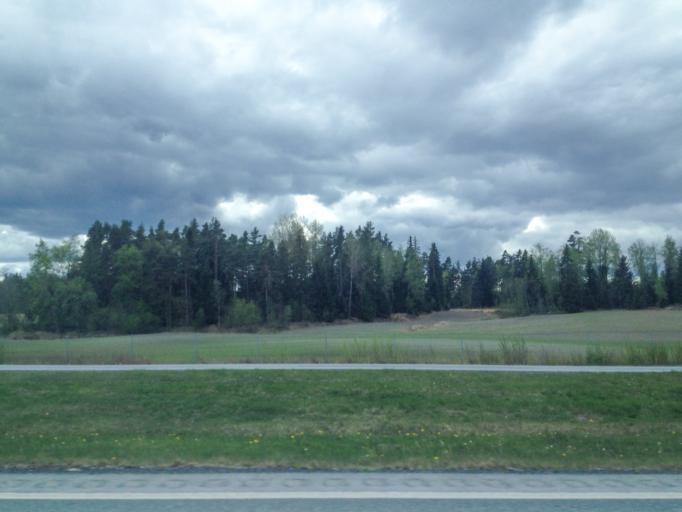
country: FI
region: Pirkanmaa
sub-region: Etelae-Pirkanmaa
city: Akaa
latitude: 61.1716
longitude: 23.9326
